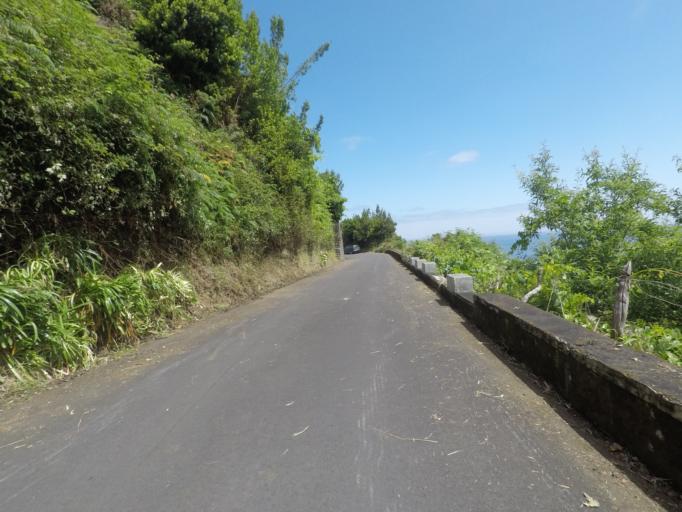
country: PT
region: Madeira
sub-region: Sao Vicente
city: Sao Vicente
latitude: 32.8167
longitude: -17.0999
